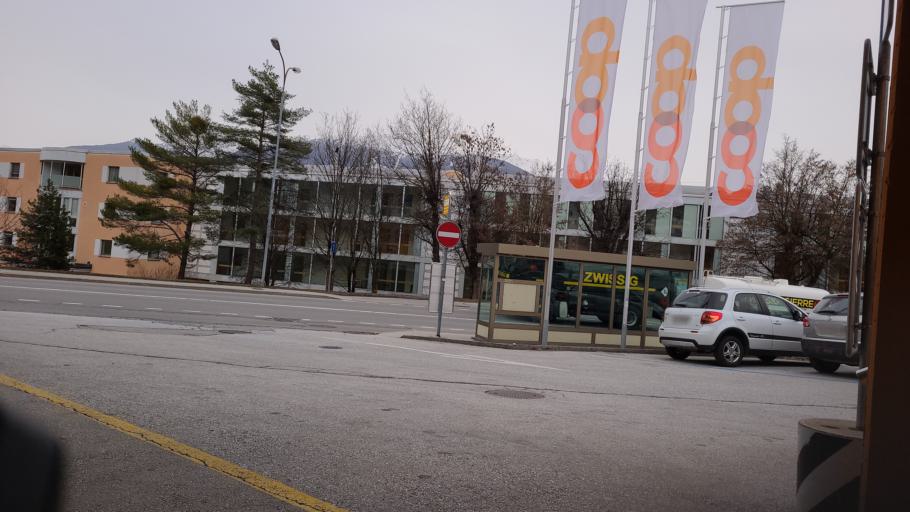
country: CH
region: Valais
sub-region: Sion District
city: Grimisuat
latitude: 46.2614
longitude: 7.3877
